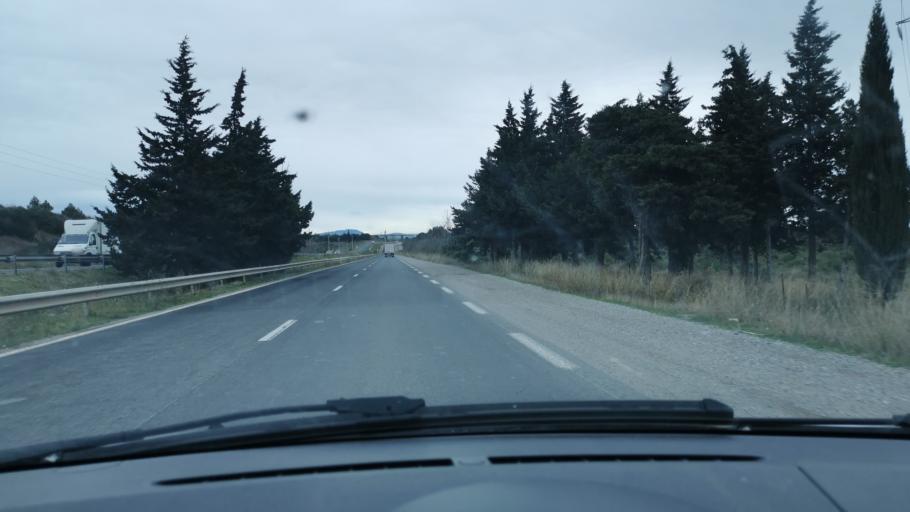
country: FR
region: Languedoc-Roussillon
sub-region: Departement de l'Herault
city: Mireval
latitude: 43.5385
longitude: 3.8230
